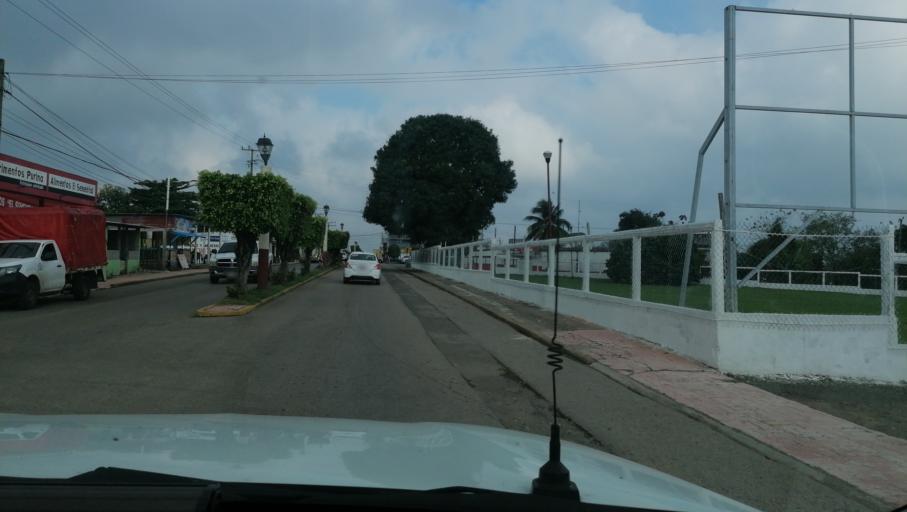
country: MX
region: Chiapas
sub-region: Juarez
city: El Triunfo 1ra. Seccion (Cardona)
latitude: 17.6041
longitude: -93.1874
